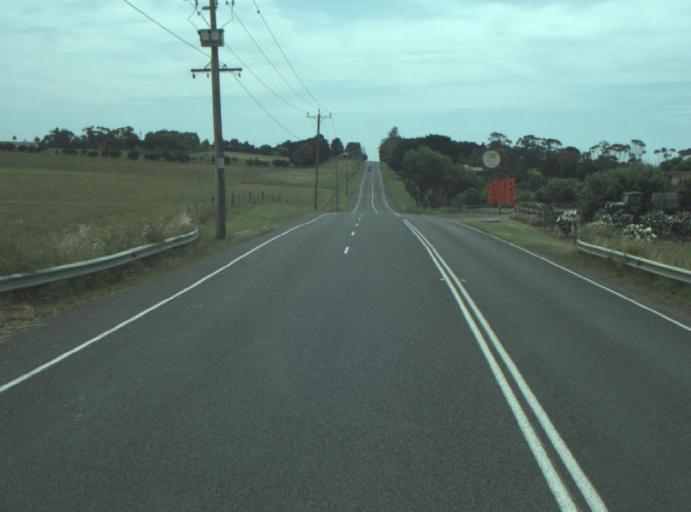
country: AU
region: Victoria
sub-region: Greater Geelong
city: Clifton Springs
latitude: -38.1382
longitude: 144.6086
